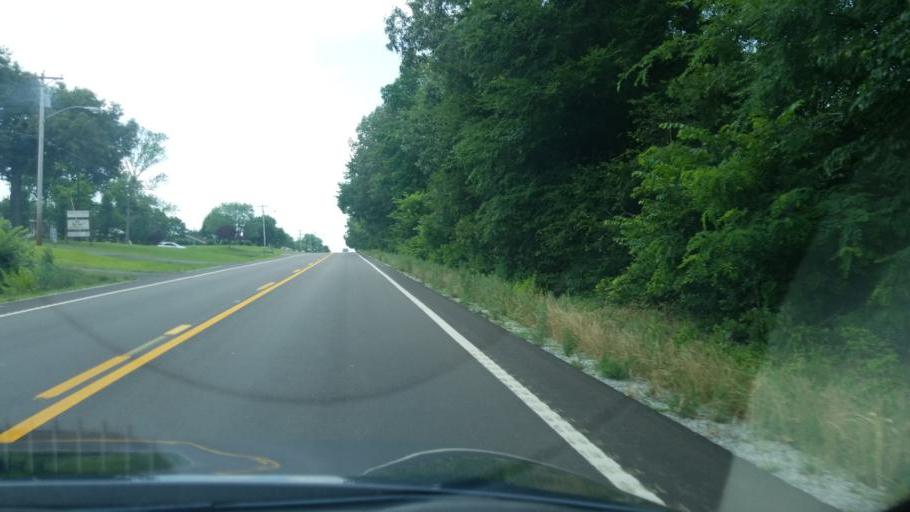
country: US
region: Tennessee
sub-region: Carroll County
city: Huntingdon
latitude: 36.0217
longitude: -88.3710
